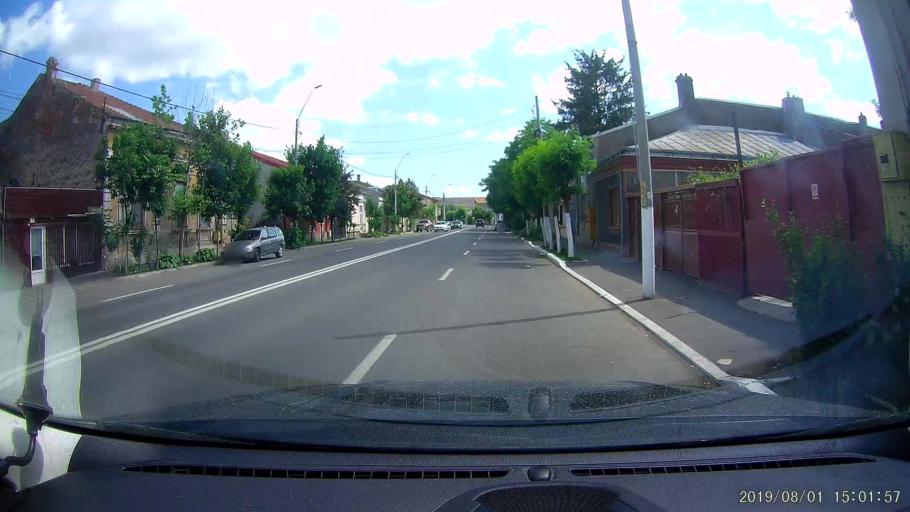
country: RO
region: Braila
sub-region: Municipiul Braila
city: Braila
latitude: 45.2700
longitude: 27.9604
